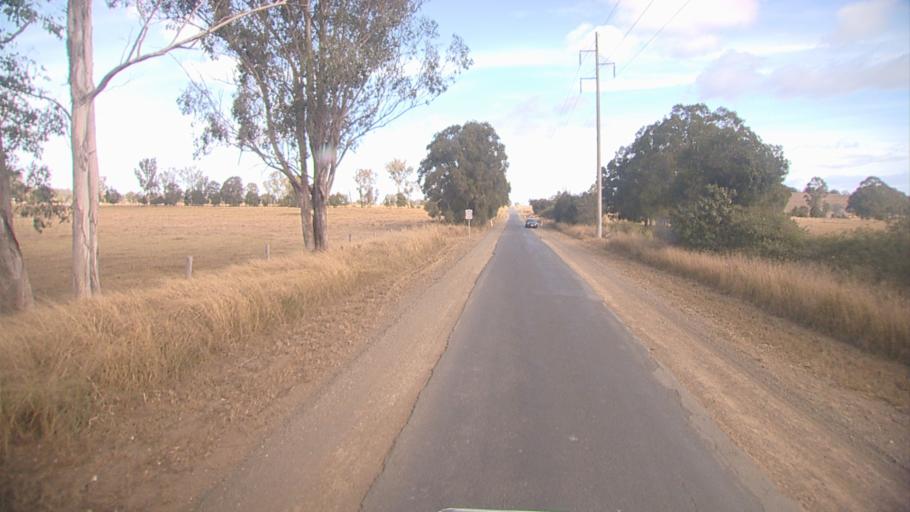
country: AU
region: Queensland
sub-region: Logan
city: Cedar Vale
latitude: -27.9183
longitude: 153.0132
